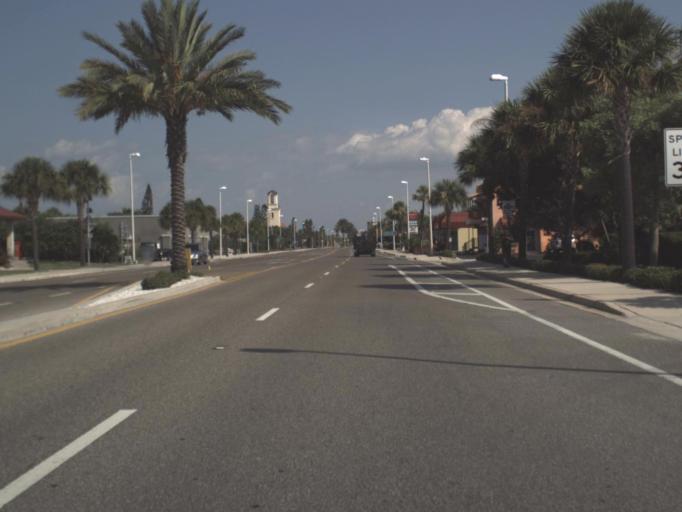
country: US
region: Florida
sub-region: Pinellas County
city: South Pasadena
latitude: 27.7445
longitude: -82.7515
